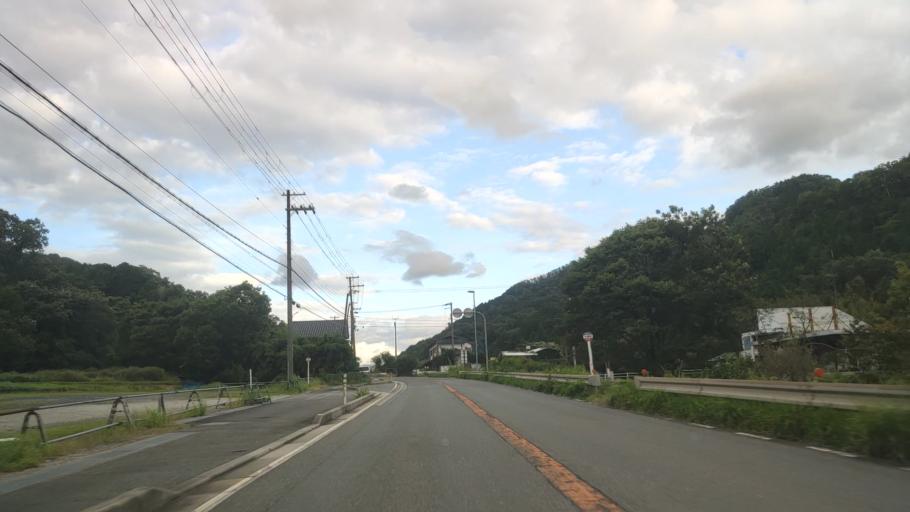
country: JP
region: Hyogo
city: Toyooka
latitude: 35.3717
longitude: 134.7921
